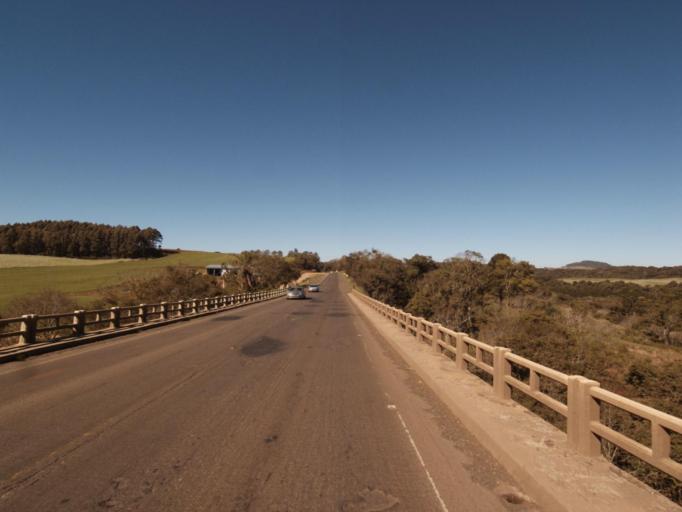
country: BR
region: Santa Catarina
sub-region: Sao Lourenco Do Oeste
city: Sao Lourenco dOeste
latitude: -26.7982
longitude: -53.1916
